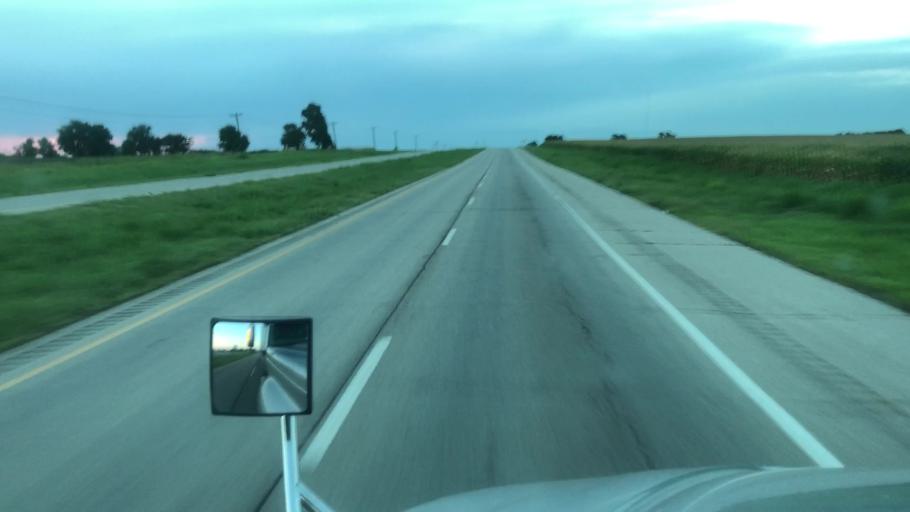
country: US
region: Oklahoma
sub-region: Kay County
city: Newkirk
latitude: 36.7994
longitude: -97.0673
